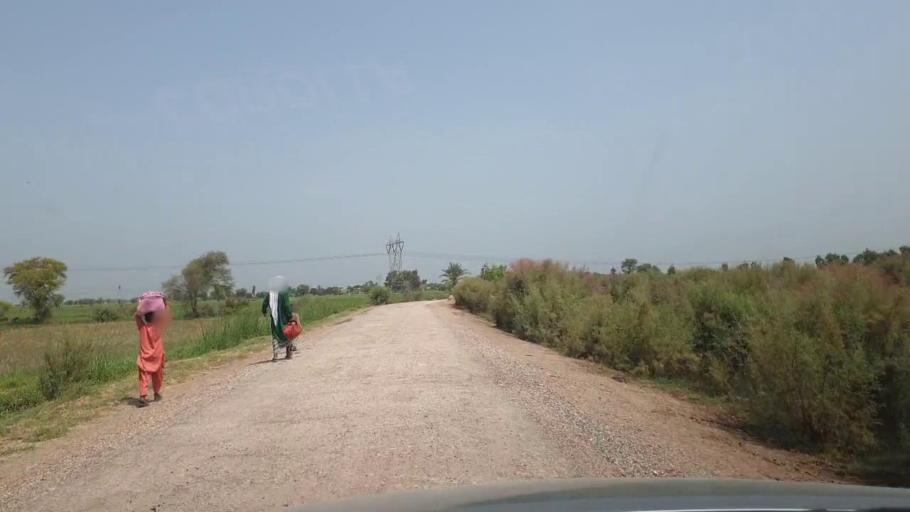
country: PK
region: Sindh
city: Madeji
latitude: 27.8027
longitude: 68.5204
